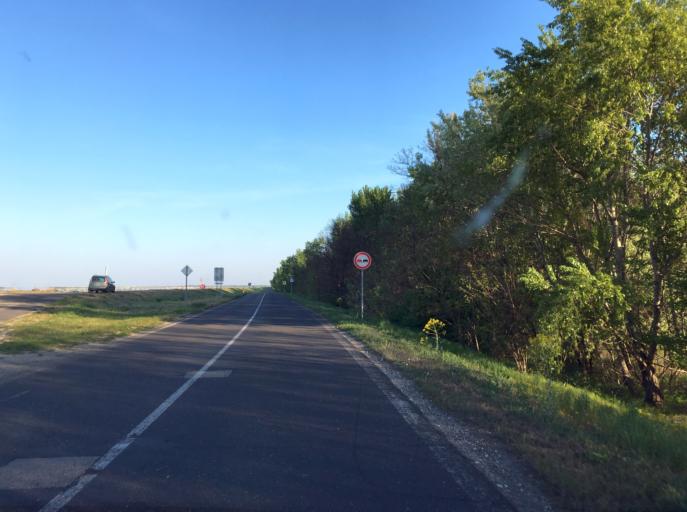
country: HU
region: Gyor-Moson-Sopron
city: Rajka
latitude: 48.0329
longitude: 17.2342
